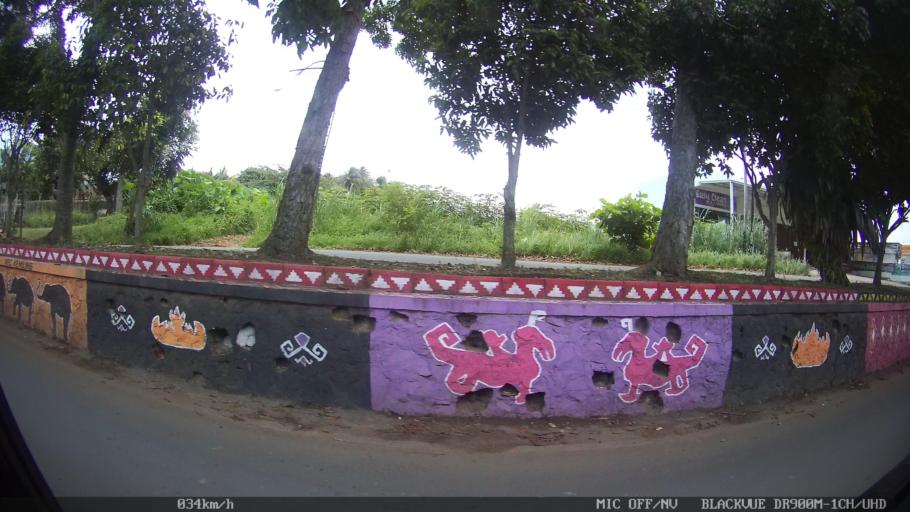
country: ID
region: Lampung
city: Bandarlampung
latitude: -5.4023
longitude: 105.2015
